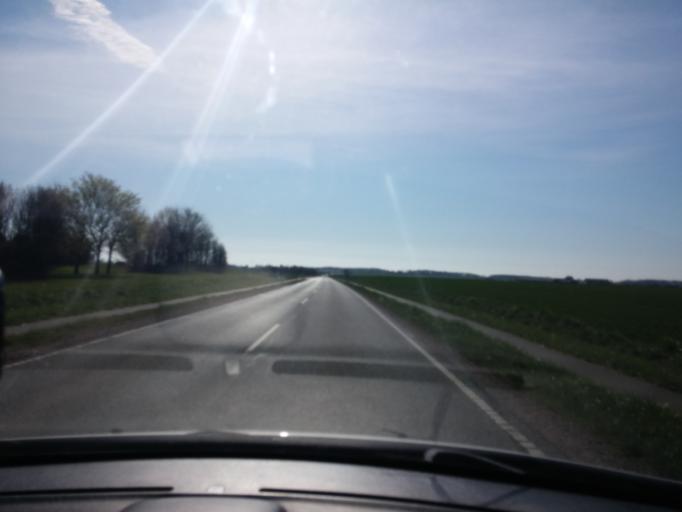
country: DK
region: Central Jutland
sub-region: Odder Kommune
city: Odder
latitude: 55.9369
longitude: 10.2186
